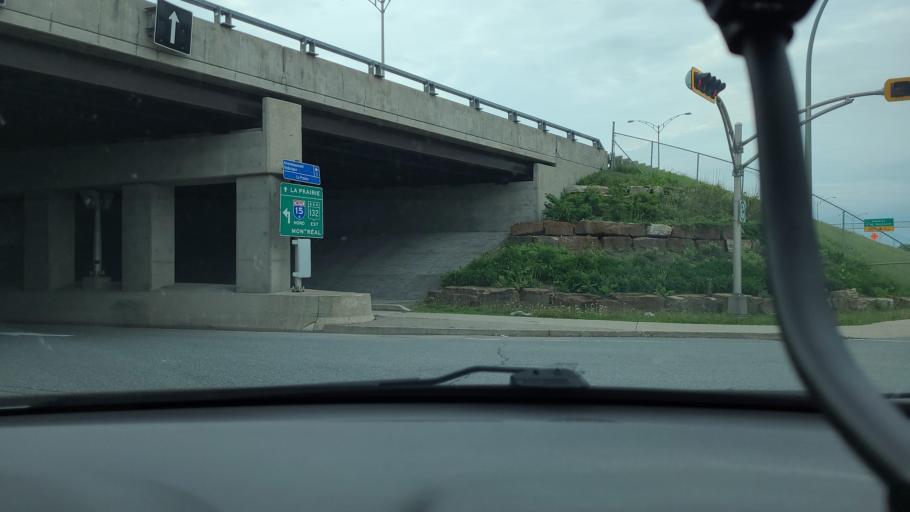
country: CA
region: Quebec
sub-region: Monteregie
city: La Prairie
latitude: 45.4083
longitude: -73.5063
